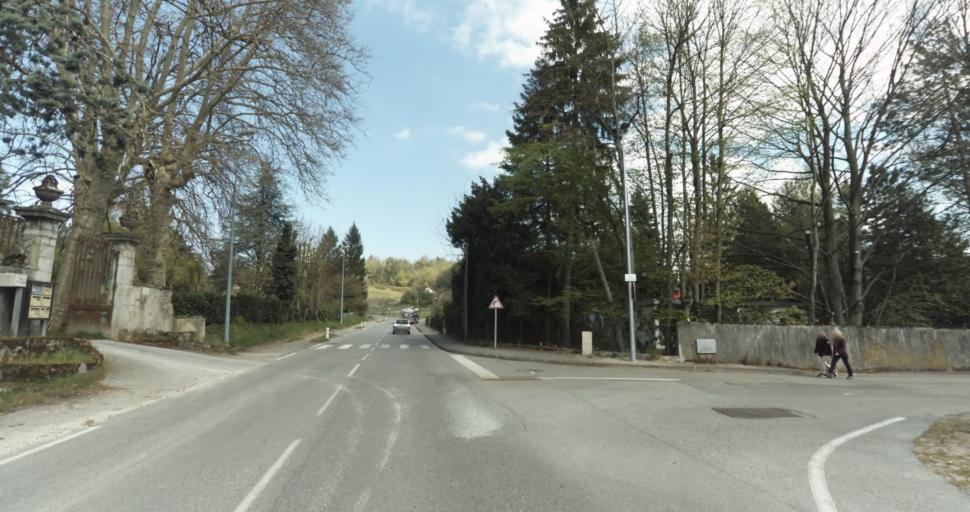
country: FR
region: Rhone-Alpes
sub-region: Departement de l'Isere
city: Saint-Marcellin
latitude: 45.1610
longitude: 5.3194
